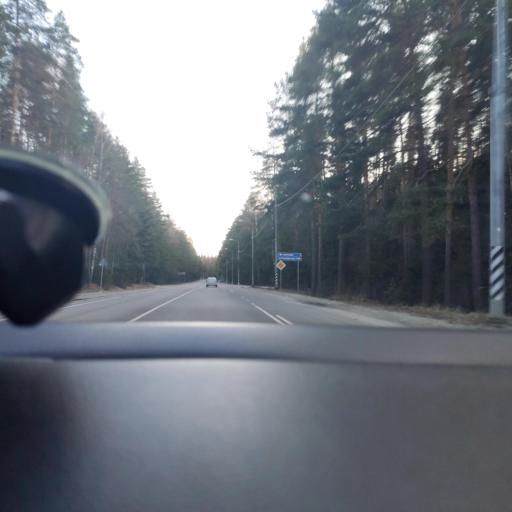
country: RU
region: Moskovskaya
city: Krasnyy Tkach
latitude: 55.4141
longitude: 39.1734
